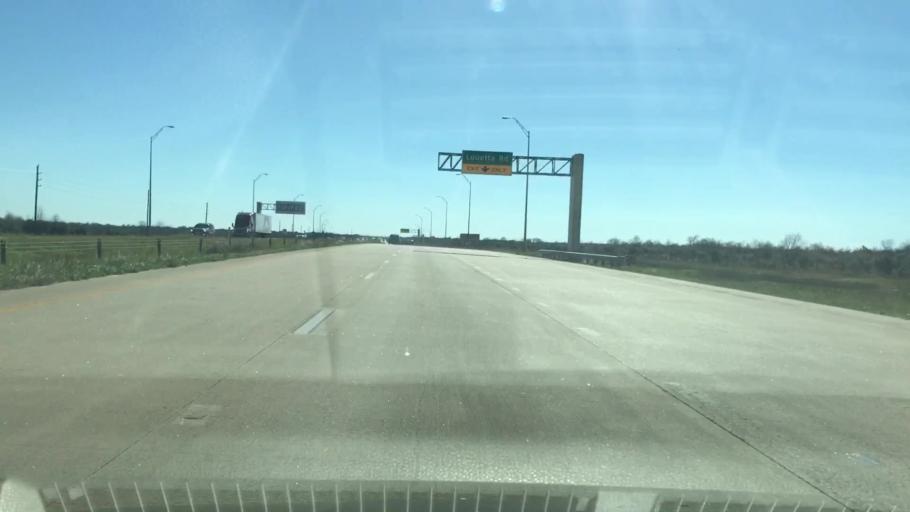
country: US
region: Texas
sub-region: Harris County
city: Cypress
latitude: 29.9873
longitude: -95.7696
